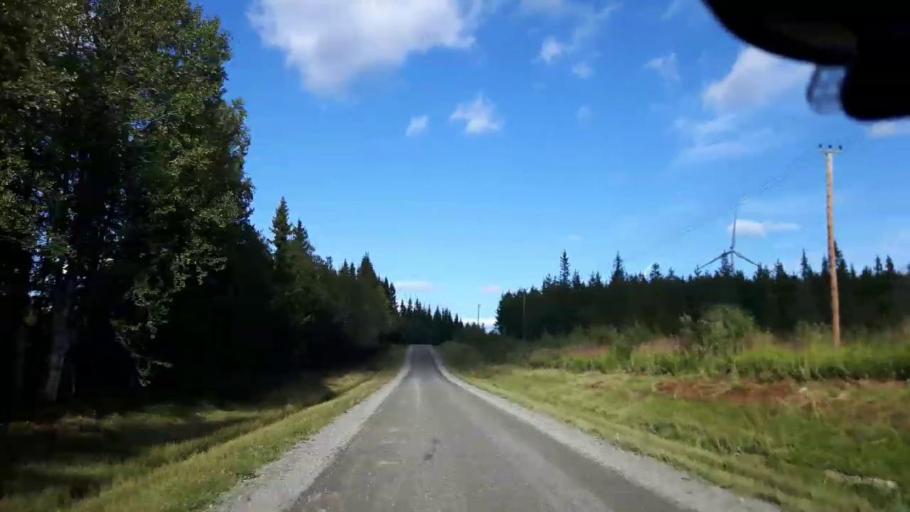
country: SE
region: Jaemtland
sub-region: Ragunda Kommun
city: Hammarstrand
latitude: 63.4165
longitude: 16.1048
